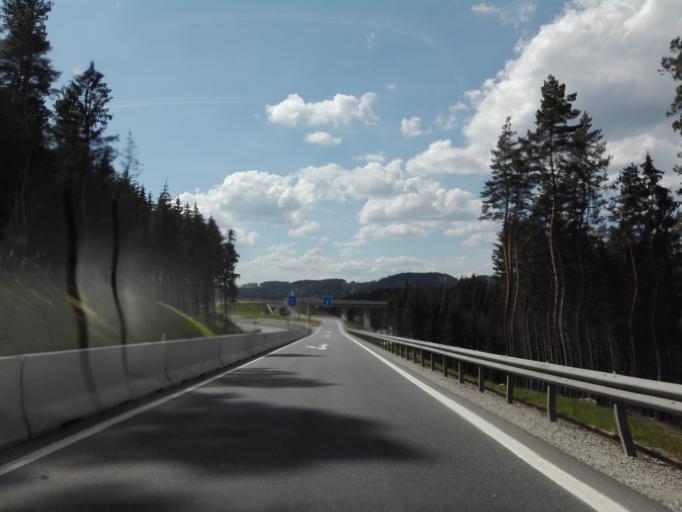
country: AT
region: Upper Austria
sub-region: Politischer Bezirk Freistadt
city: Freistadt
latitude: 48.5179
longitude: 14.5201
